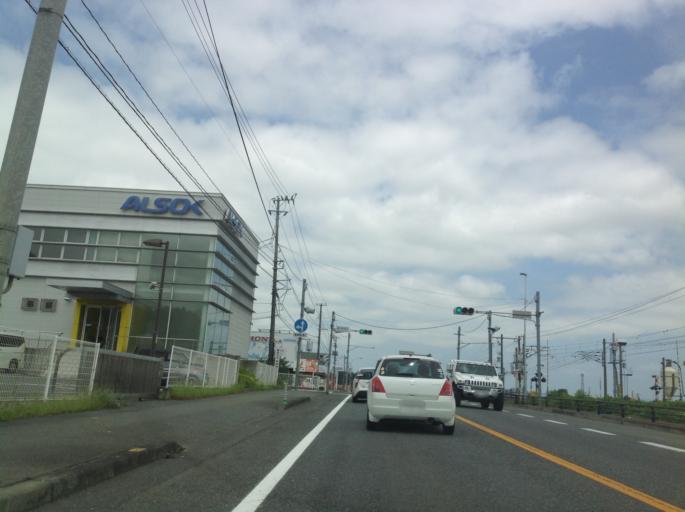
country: JP
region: Iwate
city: Mizusawa
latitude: 39.1195
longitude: 141.1464
